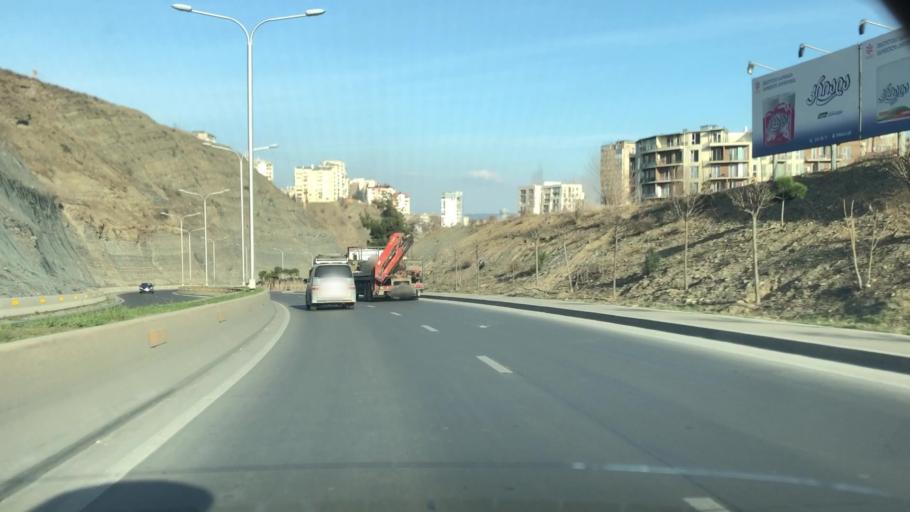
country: GE
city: Tsqnet'i
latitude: 41.7157
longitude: 44.7541
